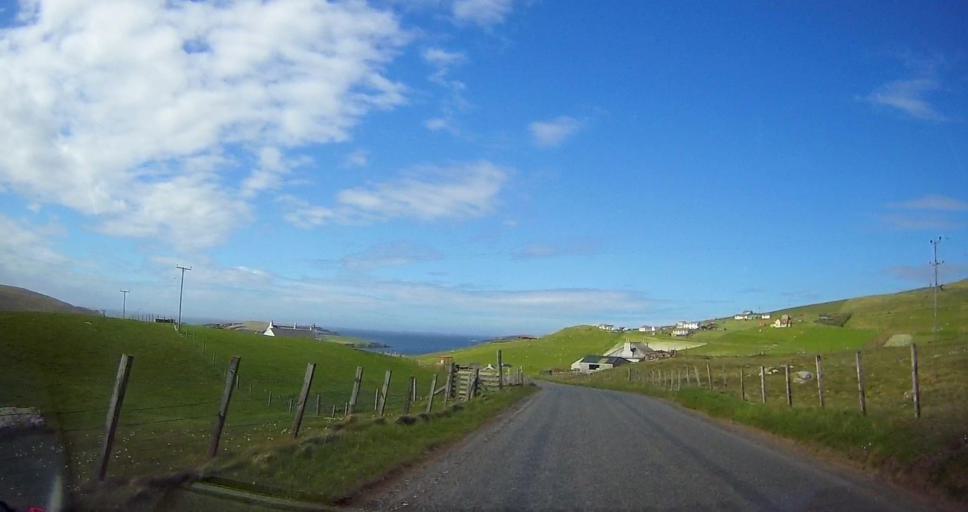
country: GB
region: Scotland
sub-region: Shetland Islands
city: Sandwick
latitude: 59.9387
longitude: -1.3221
